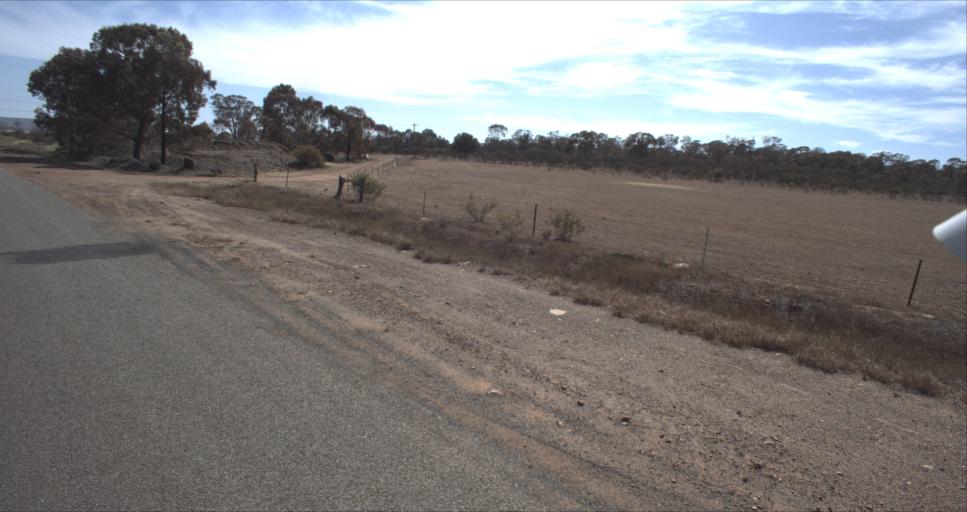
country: AU
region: New South Wales
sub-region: Leeton
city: Leeton
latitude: -34.5820
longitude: 146.4770
